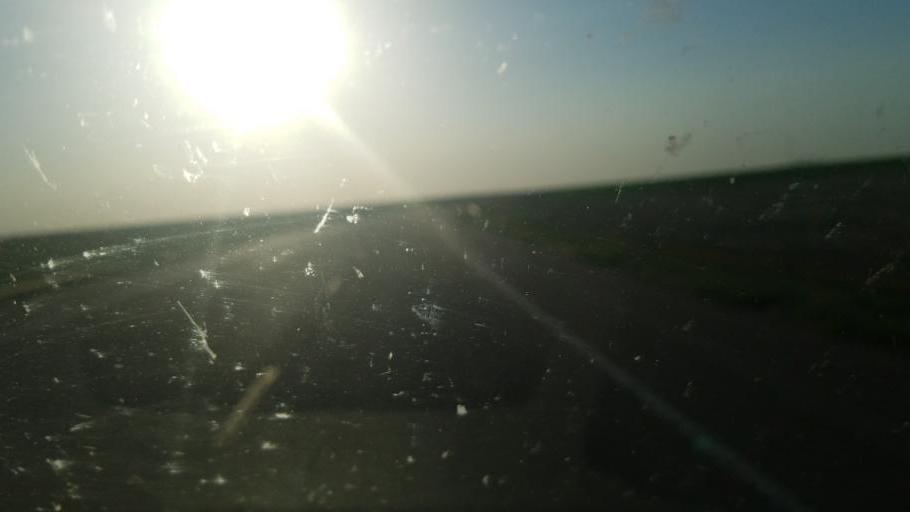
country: US
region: Kansas
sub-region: Finney County
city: Garden City
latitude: 38.0573
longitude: -100.7012
